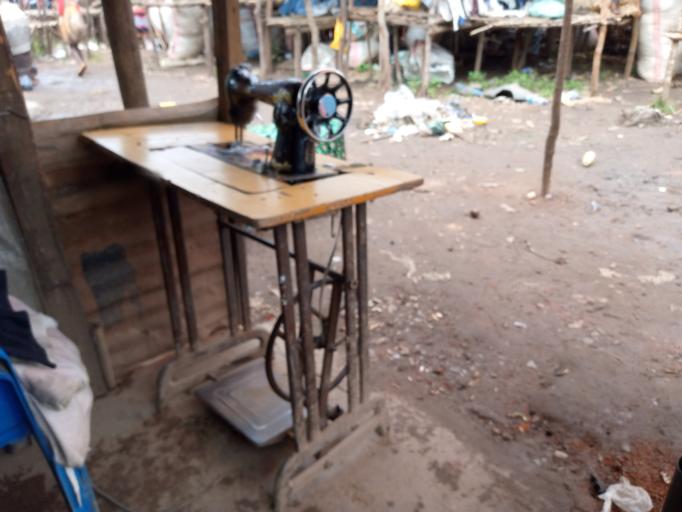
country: CD
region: Katanga
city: Lubumbashi
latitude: -11.6270
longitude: 27.4948
